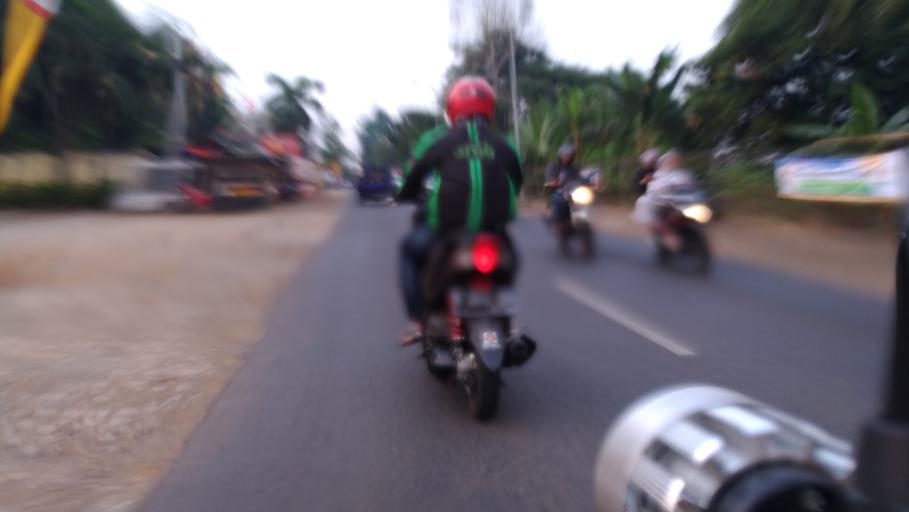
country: ID
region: West Java
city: Depok
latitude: -6.3634
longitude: 106.8875
